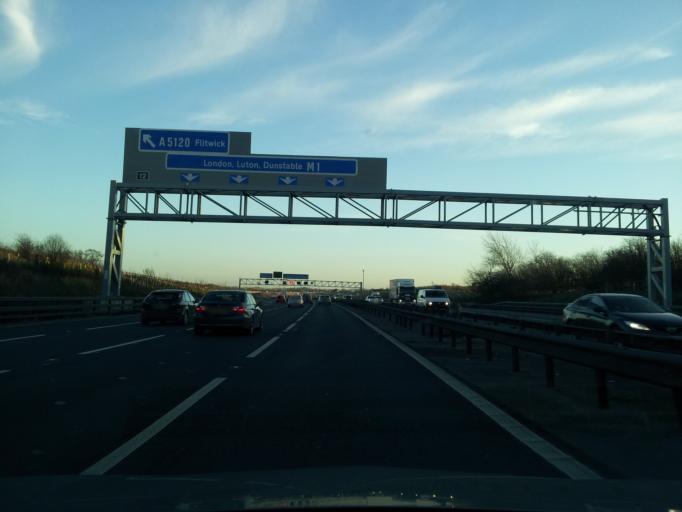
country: GB
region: England
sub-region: Central Bedfordshire
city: Toddington
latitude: 51.9655
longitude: -0.5235
